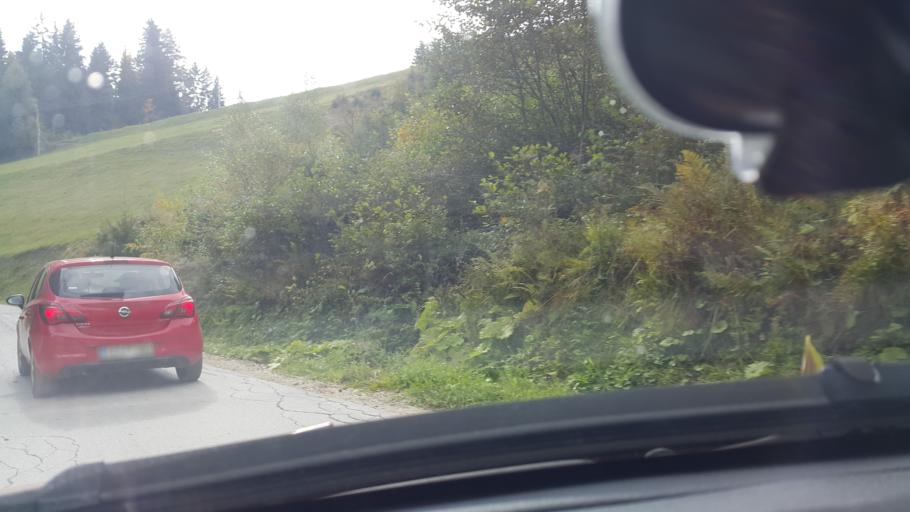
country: SI
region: Mislinja
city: Mislinja
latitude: 46.4244
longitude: 15.2703
